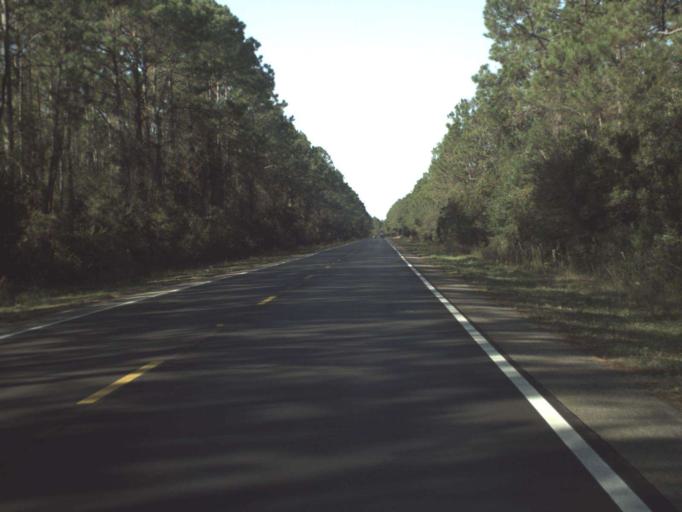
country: US
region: Florida
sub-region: Gulf County
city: Port Saint Joe
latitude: 29.7655
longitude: -85.2616
